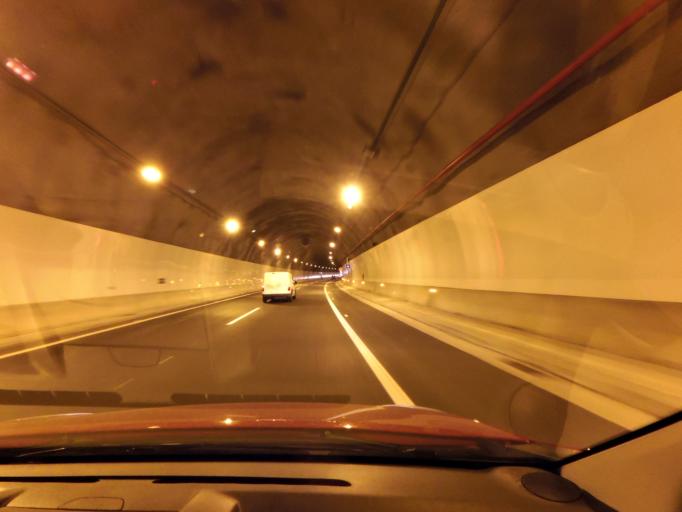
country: ES
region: Canary Islands
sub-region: Provincia de Las Palmas
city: Puerto Rico
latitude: 27.8064
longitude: -15.7107
